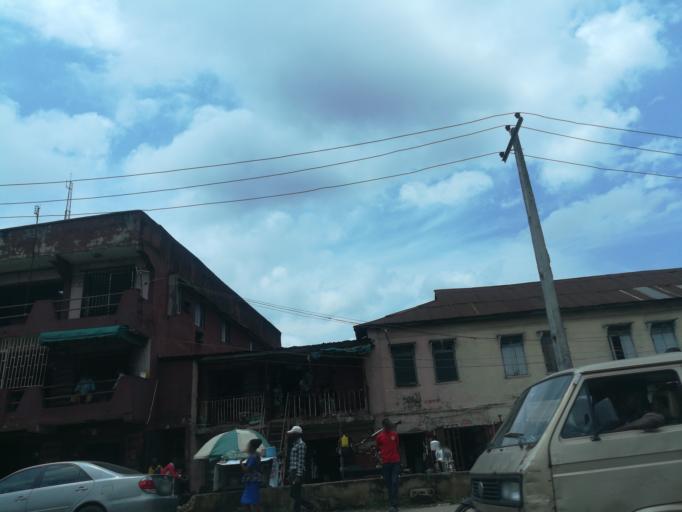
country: NG
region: Lagos
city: Mushin
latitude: 6.5258
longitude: 3.3597
